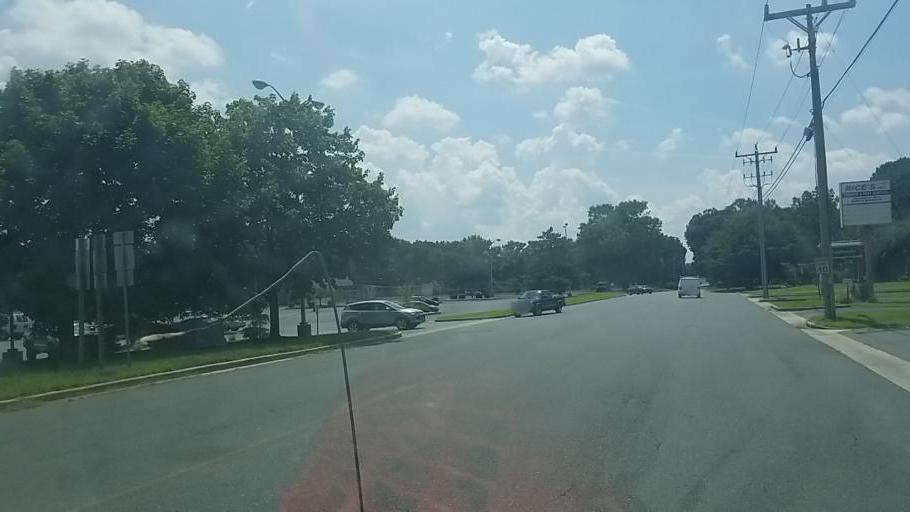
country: US
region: Maryland
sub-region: Wicomico County
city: Salisbury
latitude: 38.3649
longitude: -75.5479
